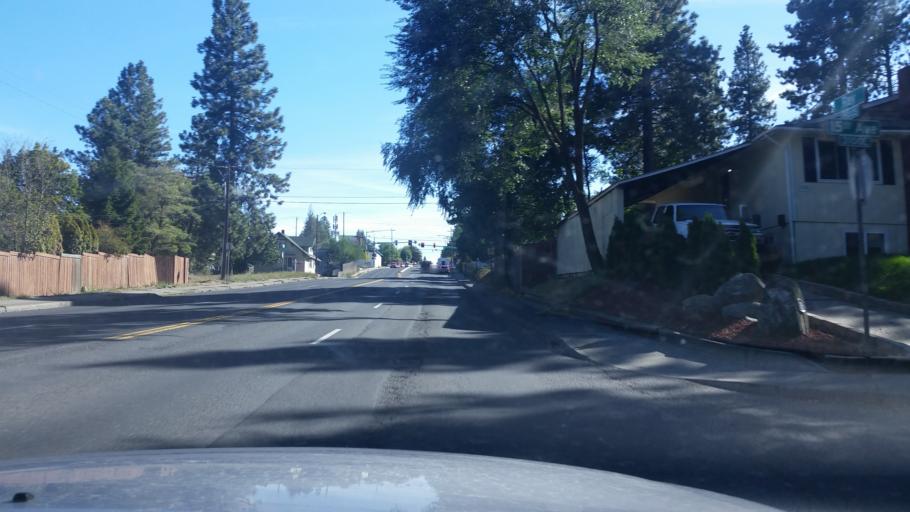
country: US
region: Washington
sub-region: Spokane County
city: Spokane
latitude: 47.6420
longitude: -117.3632
